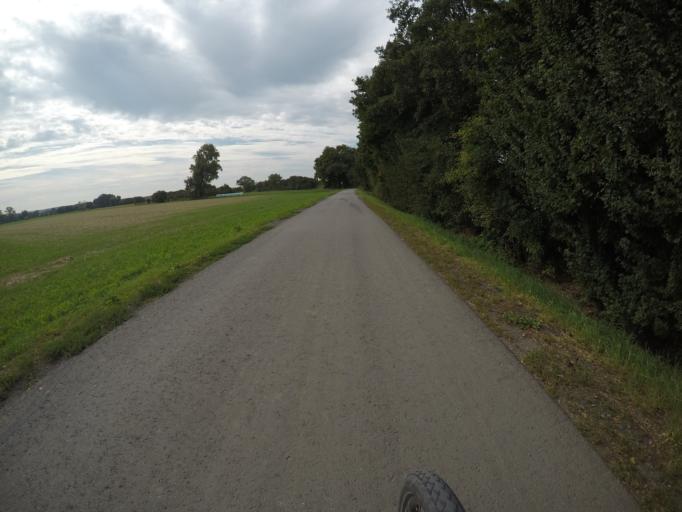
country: DE
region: Baden-Wuerttemberg
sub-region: Karlsruhe Region
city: Kronau
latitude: 49.2343
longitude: 8.6317
